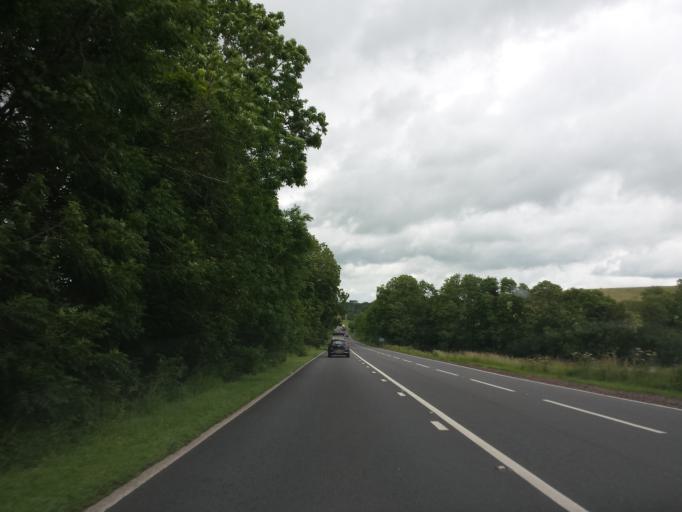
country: GB
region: Scotland
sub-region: Dumfries and Galloway
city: Castle Douglas
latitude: 54.9750
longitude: -3.8931
